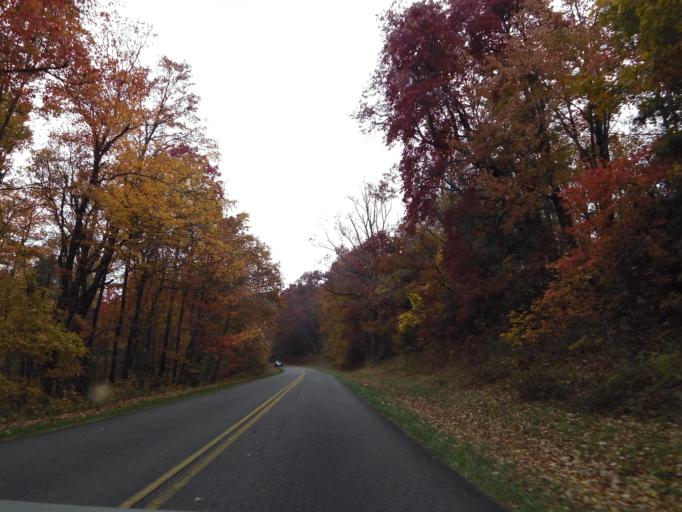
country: US
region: North Carolina
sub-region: Ashe County
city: West Jefferson
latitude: 36.2774
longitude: -81.4216
